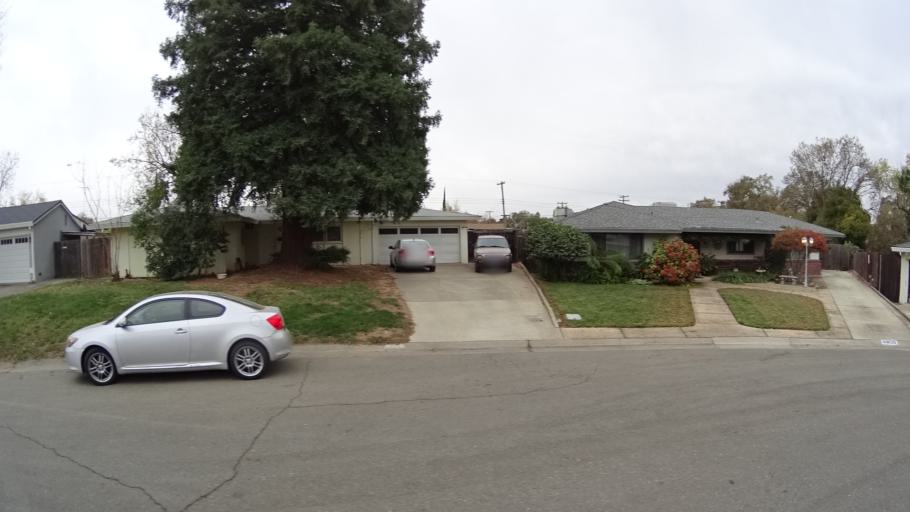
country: US
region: California
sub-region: Sacramento County
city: Antelope
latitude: 38.6987
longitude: -121.3076
